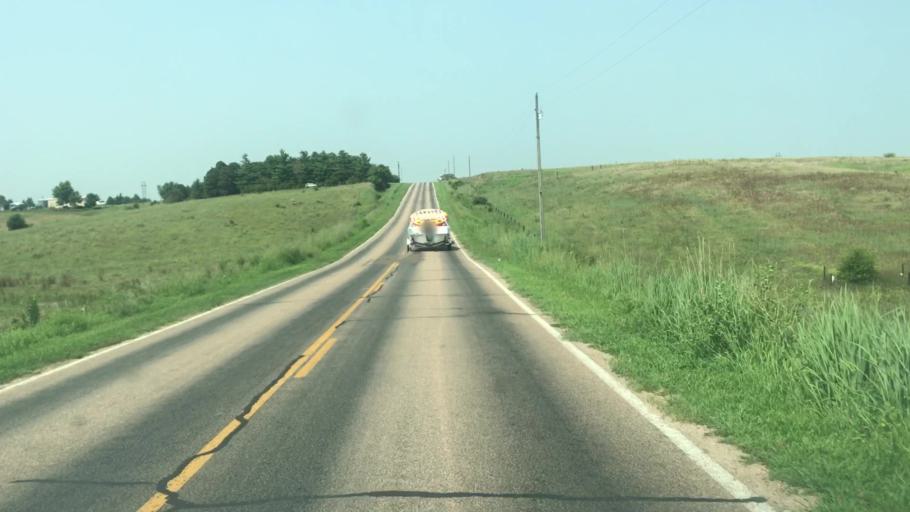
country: US
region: Nebraska
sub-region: Sherman County
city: Loup City
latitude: 41.2821
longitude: -98.8998
